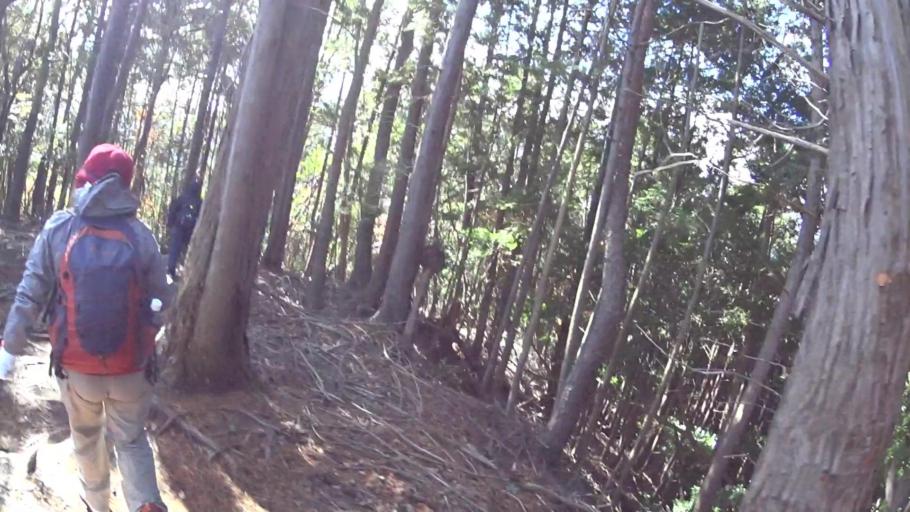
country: JP
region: Kyoto
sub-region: Kyoto-shi
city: Kamigyo-ku
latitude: 35.0911
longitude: 135.7502
